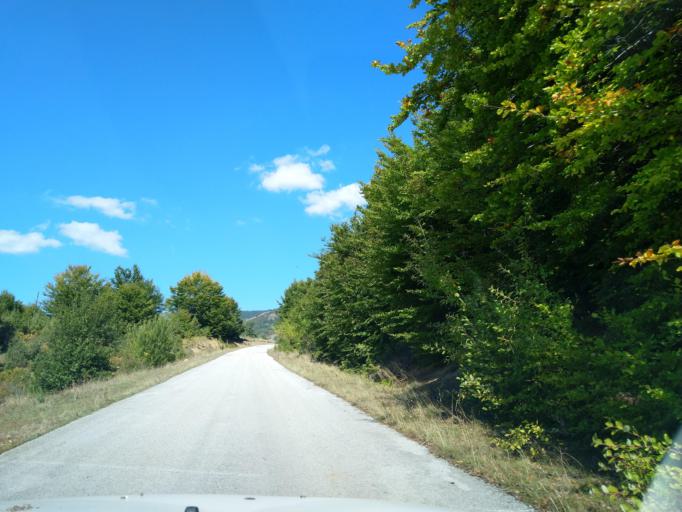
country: RS
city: Sokolovica
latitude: 43.2510
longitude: 20.3108
